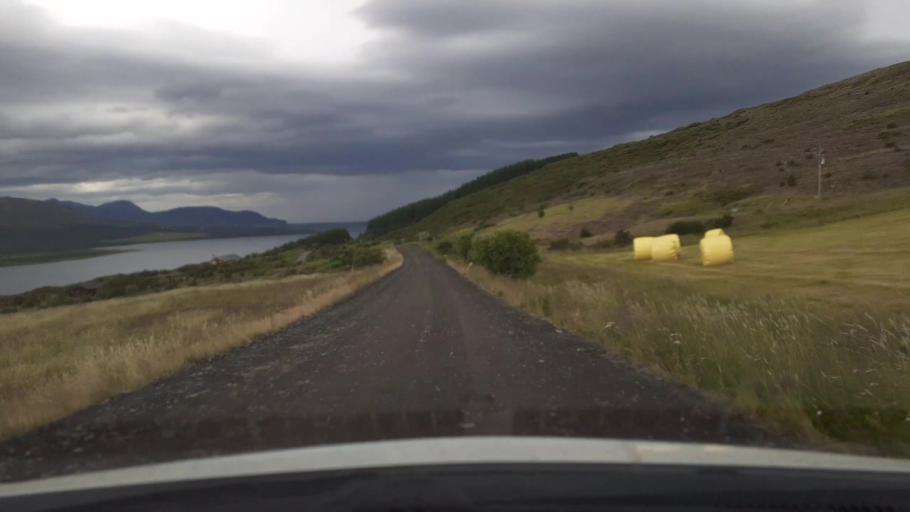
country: IS
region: Capital Region
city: Mosfellsbaer
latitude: 64.5267
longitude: -21.4863
